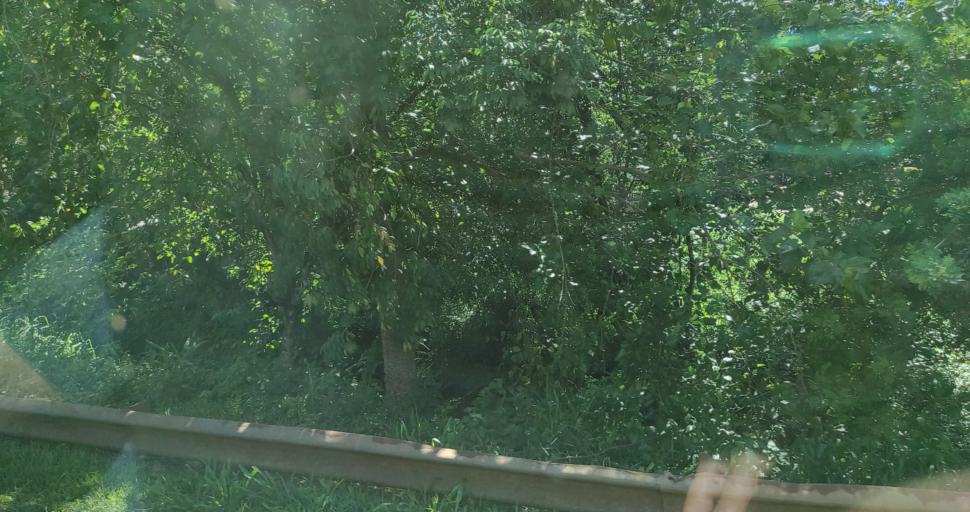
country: AR
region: Misiones
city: El Soberbio
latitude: -27.2826
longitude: -54.1967
